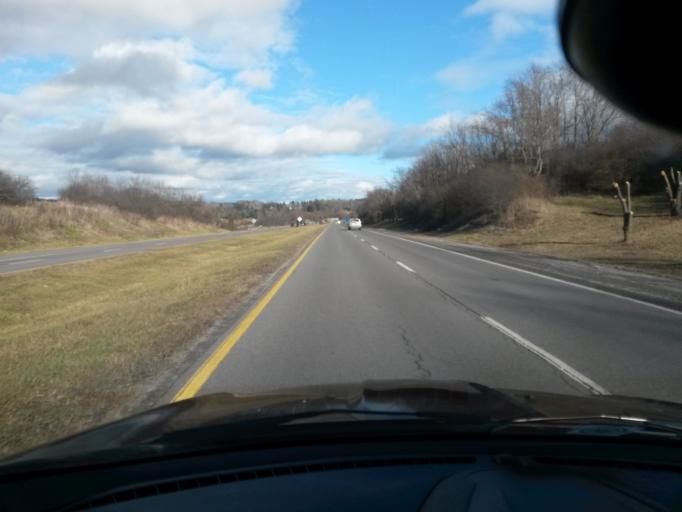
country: US
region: Virginia
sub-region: Tazewell County
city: Bluefield
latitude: 37.2382
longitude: -81.2474
